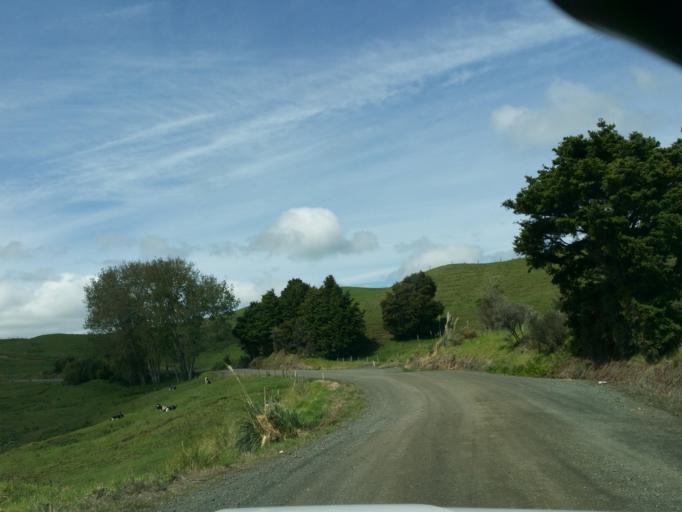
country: NZ
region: Northland
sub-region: Kaipara District
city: Dargaville
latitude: -35.8775
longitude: 174.0550
